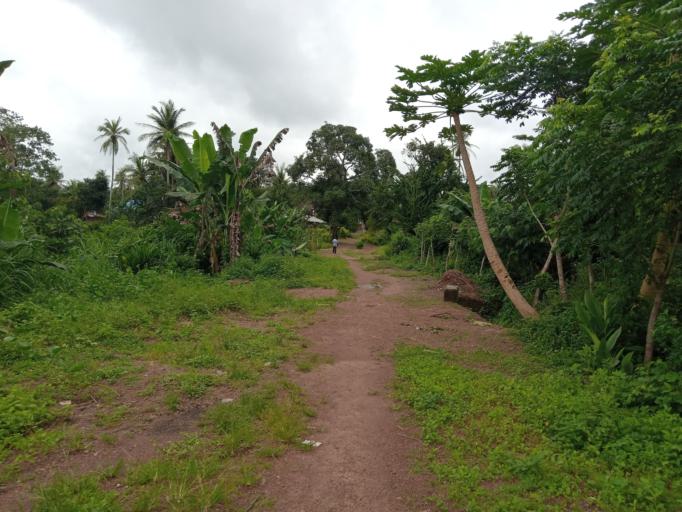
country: SL
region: Southern Province
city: Largo
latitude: 8.2051
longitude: -12.0607
